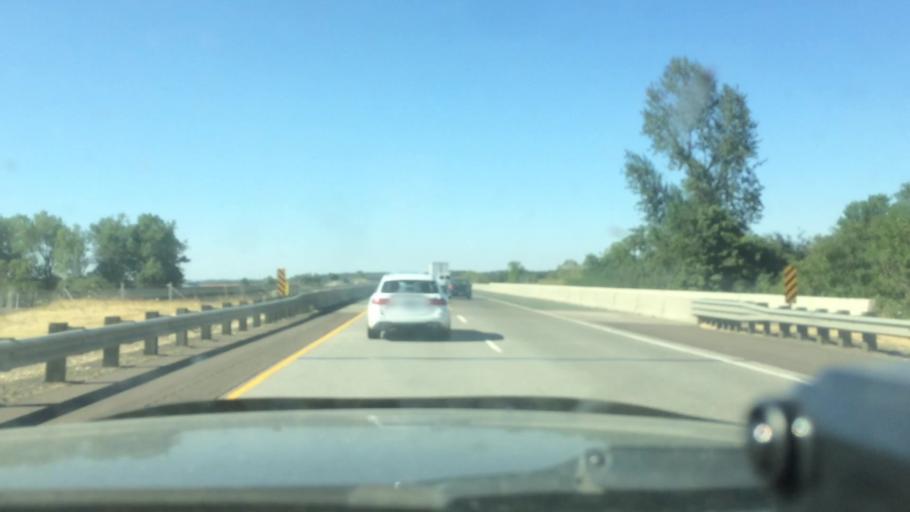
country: US
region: Oregon
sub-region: Linn County
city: Brownsville
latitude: 44.4550
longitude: -123.0609
